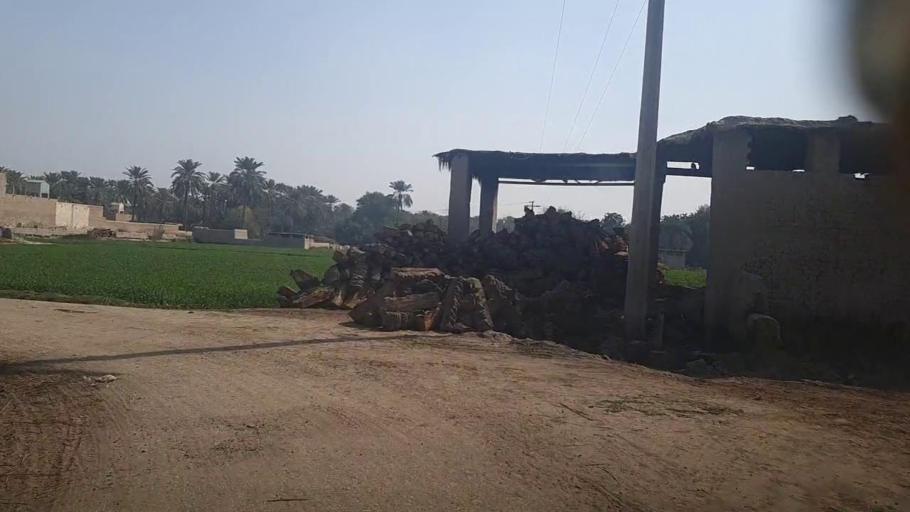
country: PK
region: Sindh
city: Khairpur
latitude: 27.5531
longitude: 68.7883
